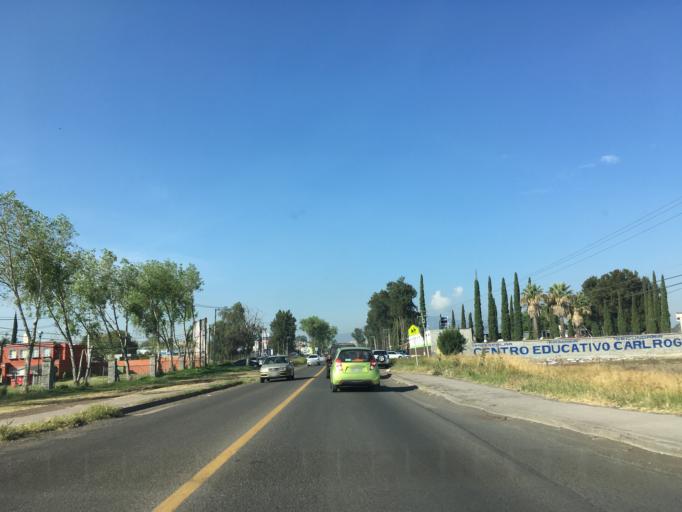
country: MX
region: Michoacan
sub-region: Tarimbaro
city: La Palma (Las Palmas)
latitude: 19.7746
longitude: -101.1371
